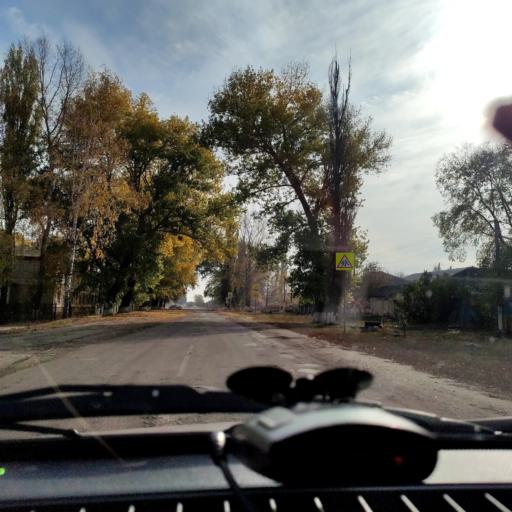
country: RU
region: Voronezj
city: Rossosh'
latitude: 51.2039
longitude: 38.7656
